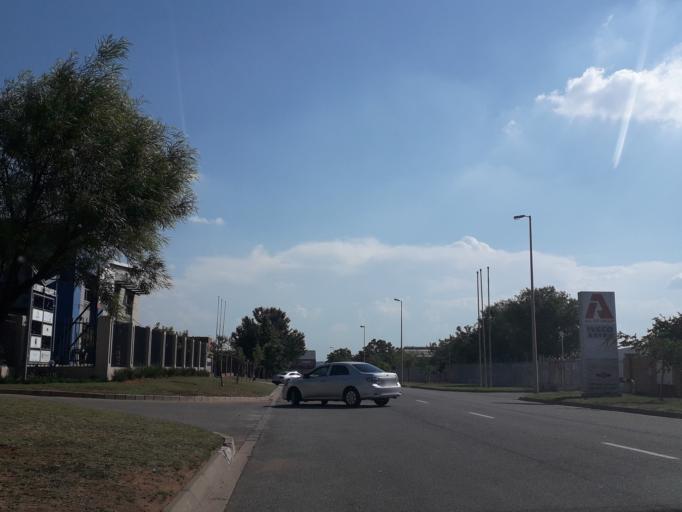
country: ZA
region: Gauteng
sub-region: City of Johannesburg Metropolitan Municipality
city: Midrand
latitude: -25.9391
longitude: 28.1422
